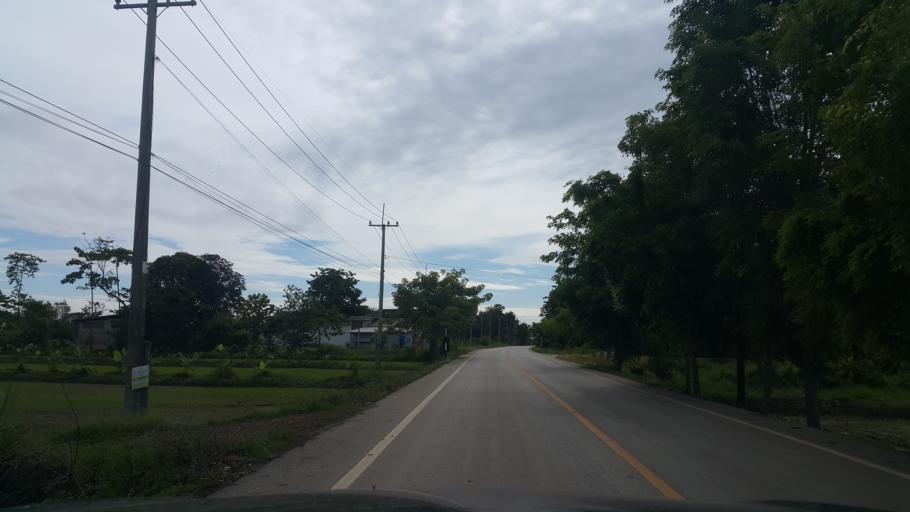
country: TH
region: Sukhothai
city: Si Nakhon
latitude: 17.2811
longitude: 100.0080
